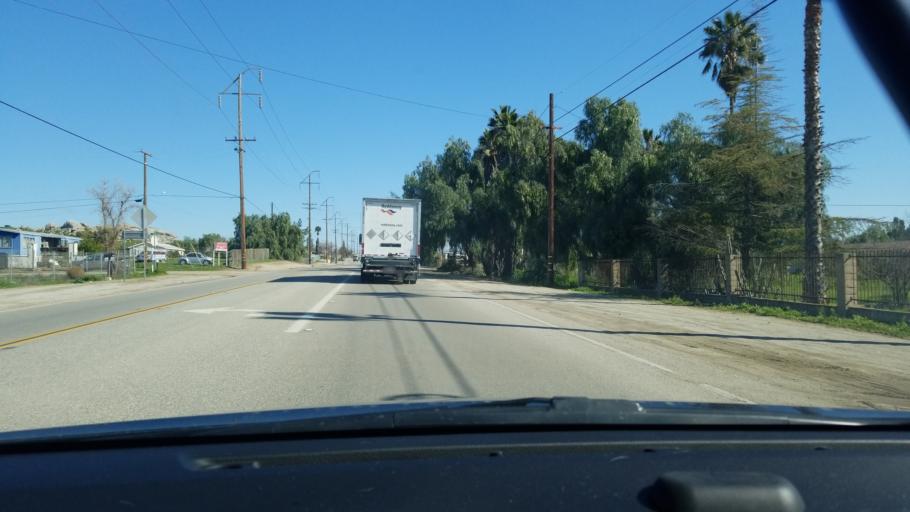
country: US
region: California
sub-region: Riverside County
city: Mead Valley
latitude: 33.8372
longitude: -117.2826
